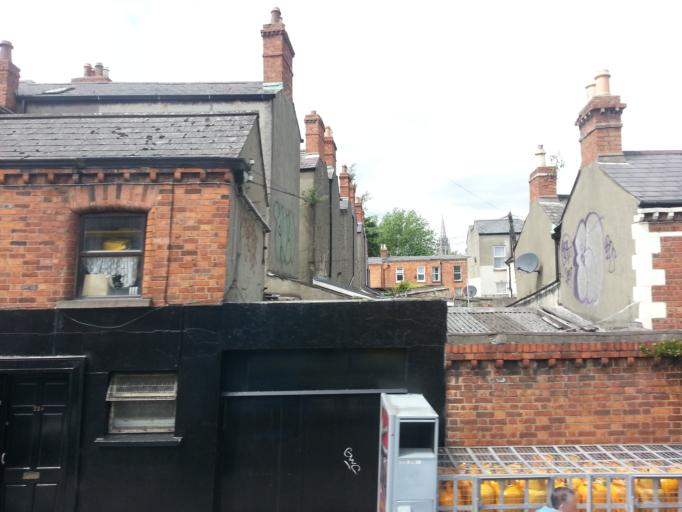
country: IE
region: Leinster
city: Drumcondra
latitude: 53.3596
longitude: -6.2698
